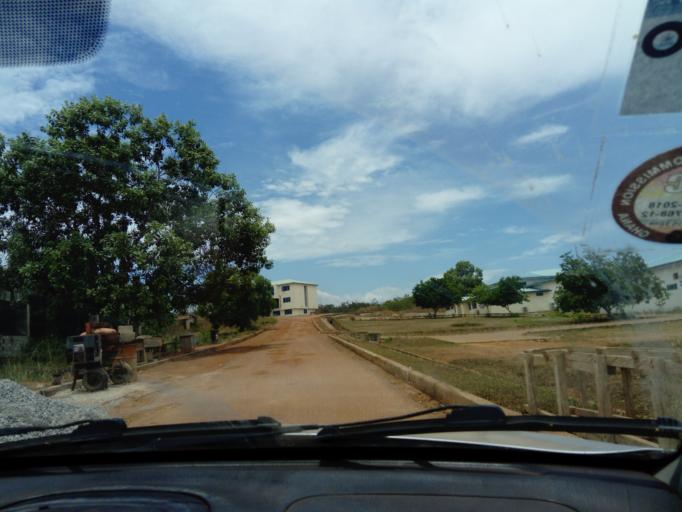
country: GH
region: Central
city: Cape Coast
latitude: 5.1363
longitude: -1.2846
